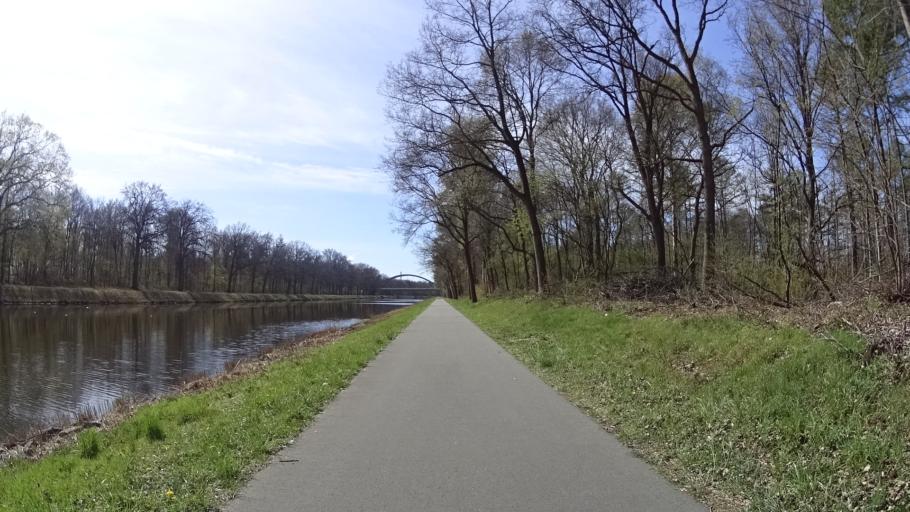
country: DE
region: Lower Saxony
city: Geeste
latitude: 52.5754
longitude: 7.3106
